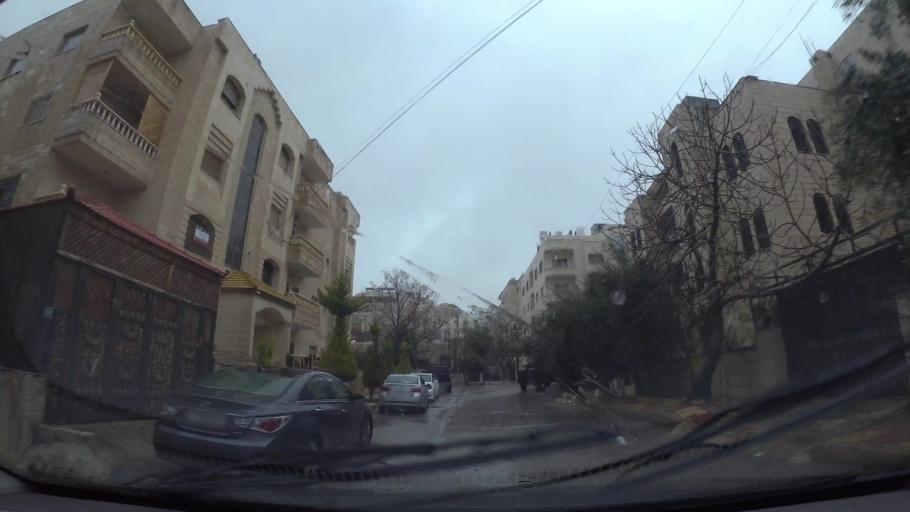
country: JO
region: Amman
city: Al Jubayhah
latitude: 32.0123
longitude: 35.8866
